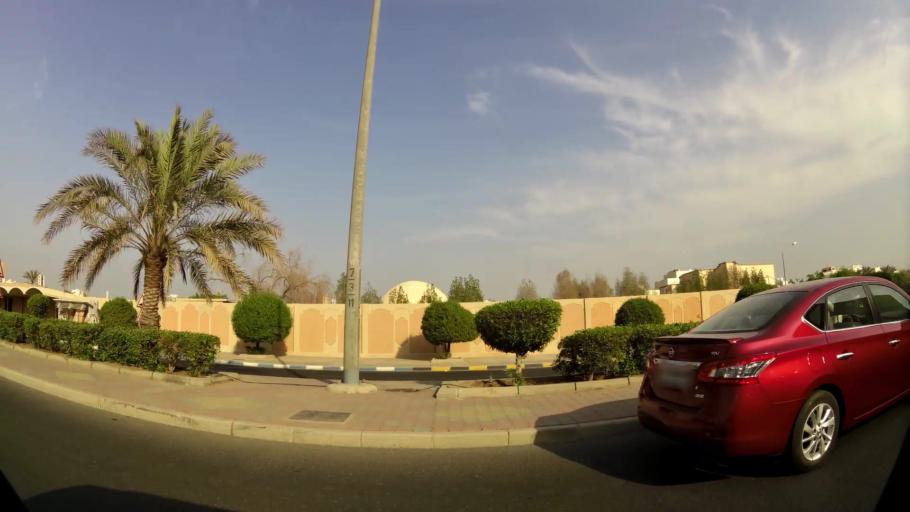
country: KW
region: Muhafazat Hawalli
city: Hawalli
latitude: 29.3283
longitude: 48.0019
